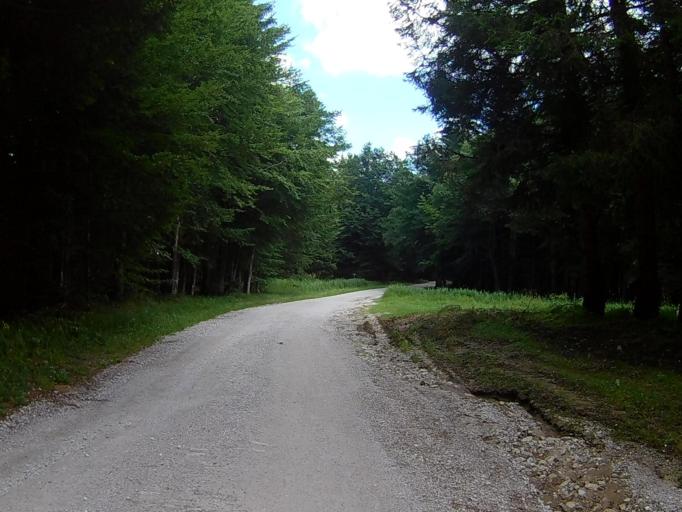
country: SI
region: Ruse
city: Ruse
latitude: 46.4977
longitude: 15.4982
